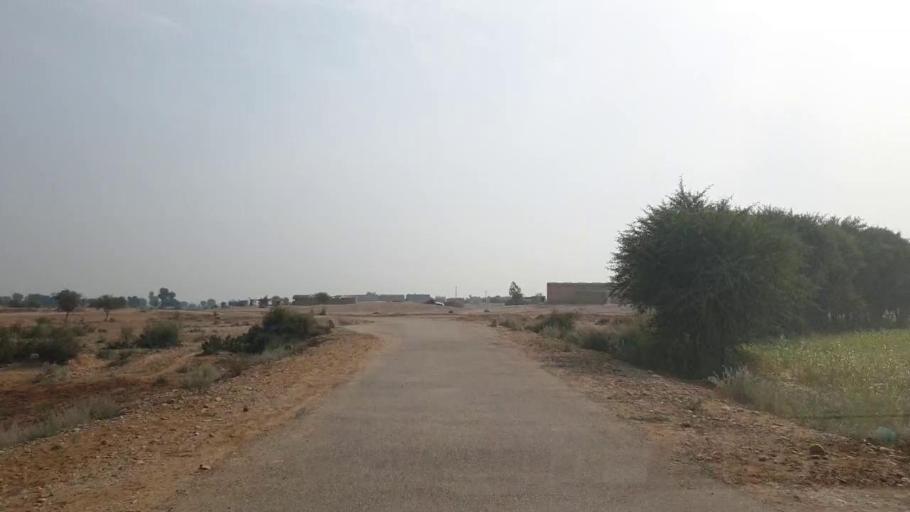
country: PK
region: Sindh
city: Sann
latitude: 26.0055
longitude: 68.1397
